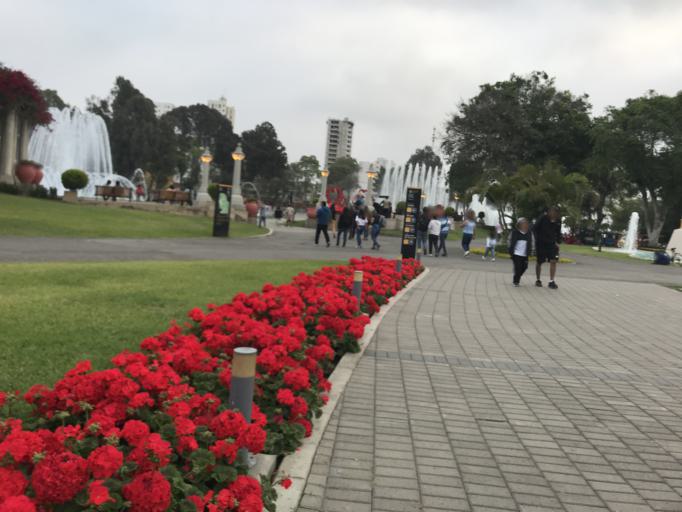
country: PE
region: Lima
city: Lima
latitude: -12.0699
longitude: -77.0333
